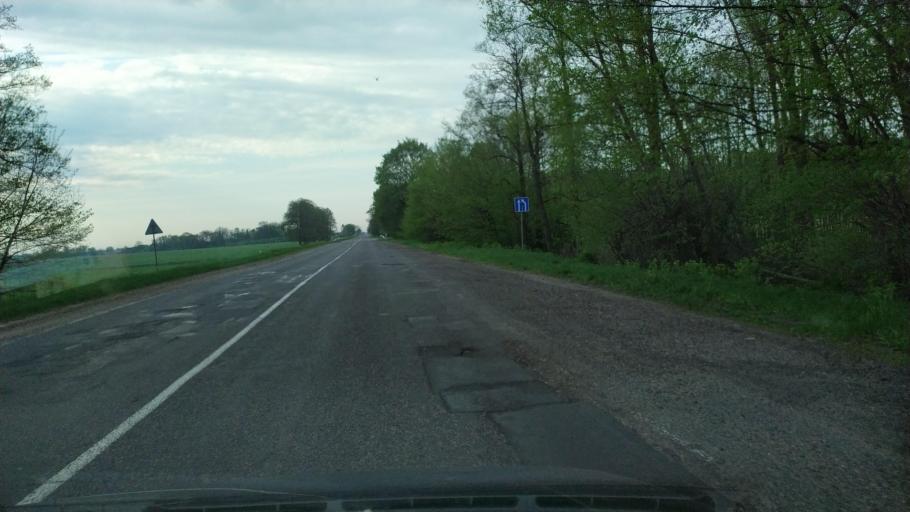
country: BY
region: Brest
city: Zhabinka
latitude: 52.2362
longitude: 23.9803
